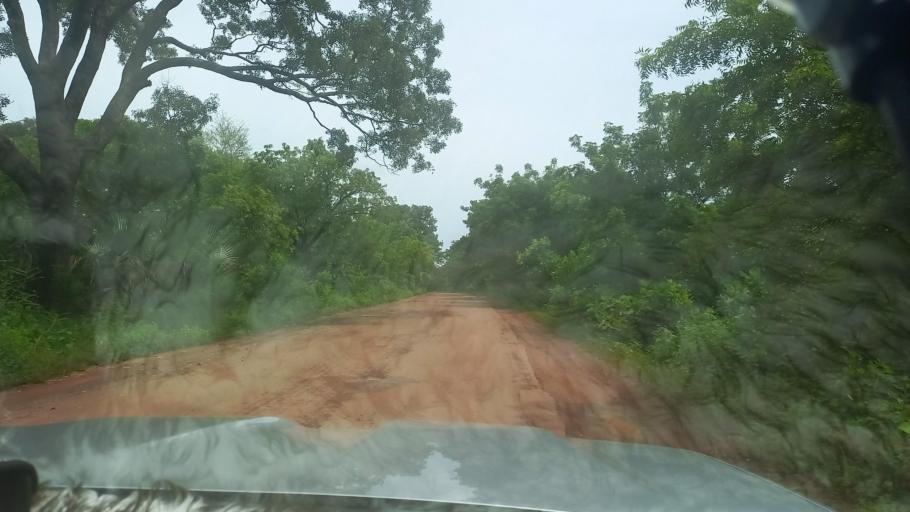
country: SN
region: Kolda
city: Marsassoum
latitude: 12.9064
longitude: -16.0163
